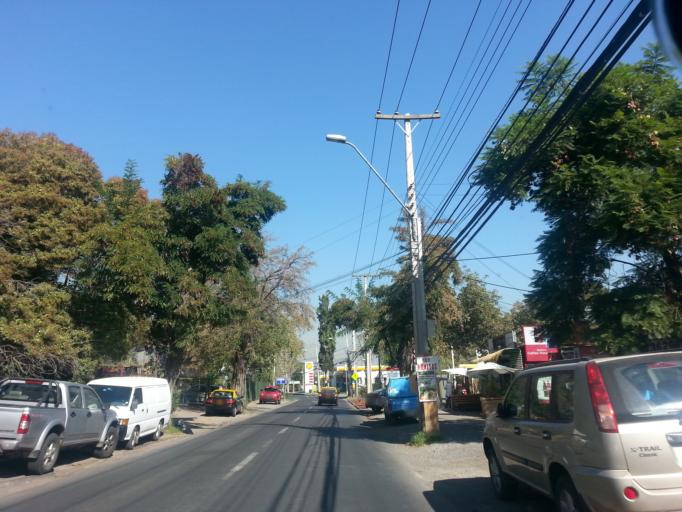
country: CL
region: Santiago Metropolitan
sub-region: Provincia de Santiago
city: Villa Presidente Frei, Nunoa, Santiago, Chile
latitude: -33.4493
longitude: -70.5439
